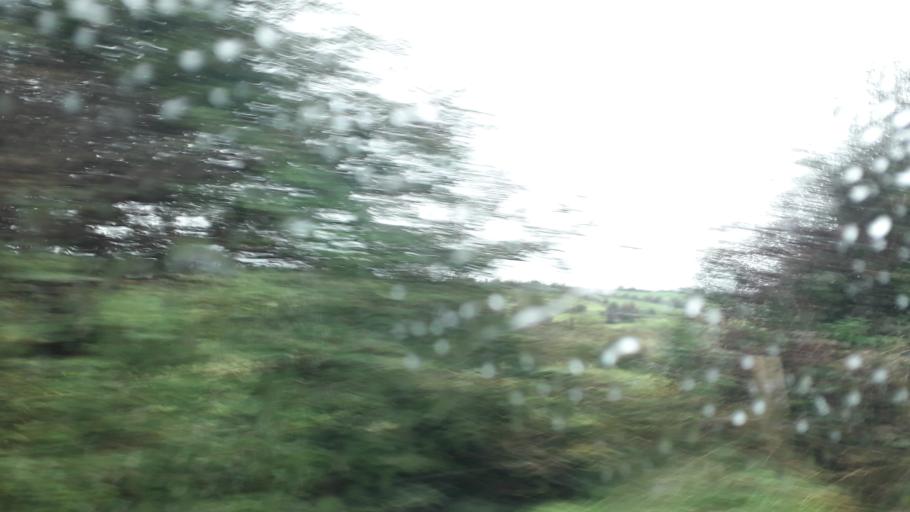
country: IE
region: Connaught
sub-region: Roscommon
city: Boyle
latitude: 53.7922
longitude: -8.2807
